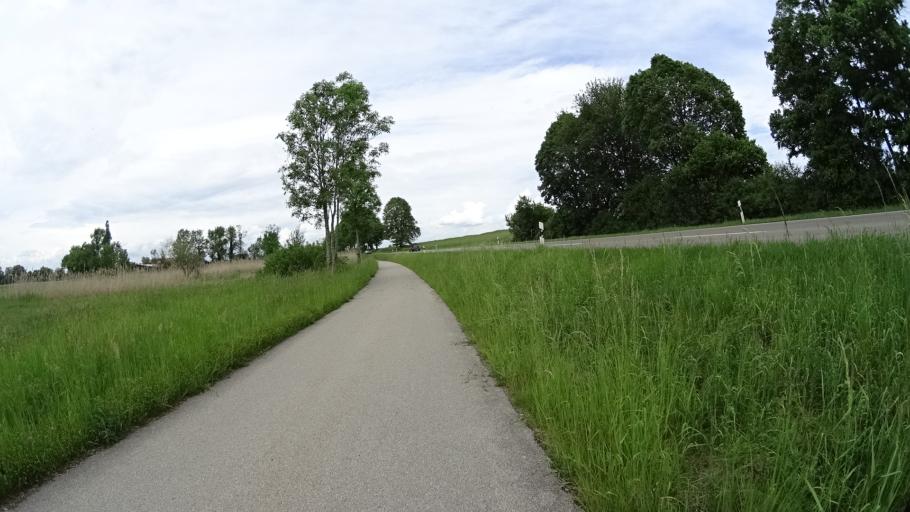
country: DE
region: Bavaria
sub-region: Swabia
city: Pfaffenhofen an der Roth
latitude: 48.3335
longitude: 10.1614
